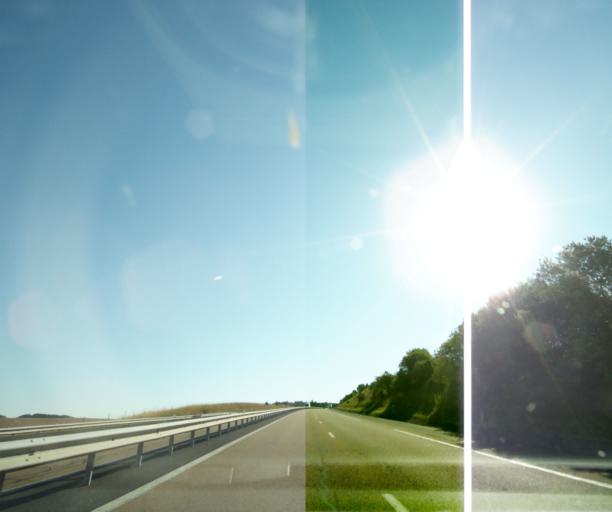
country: FR
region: Champagne-Ardenne
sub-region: Departement de l'Aube
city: Aix-en-Othe
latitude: 48.2643
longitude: 3.6829
